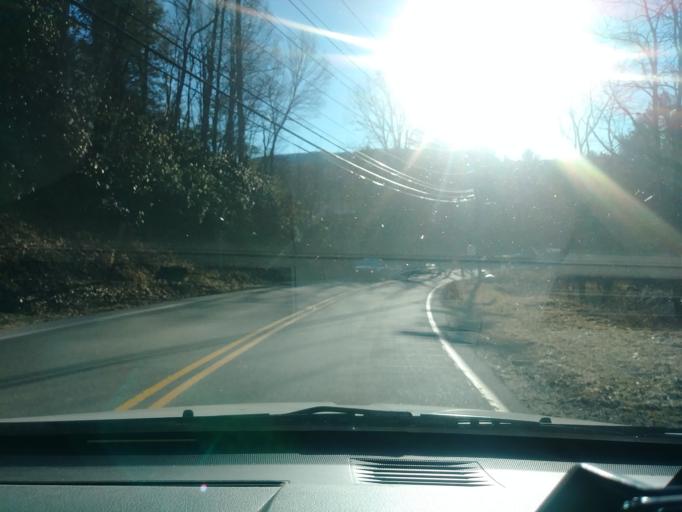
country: US
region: North Carolina
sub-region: Avery County
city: Banner Elk
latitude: 36.1592
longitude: -81.8856
